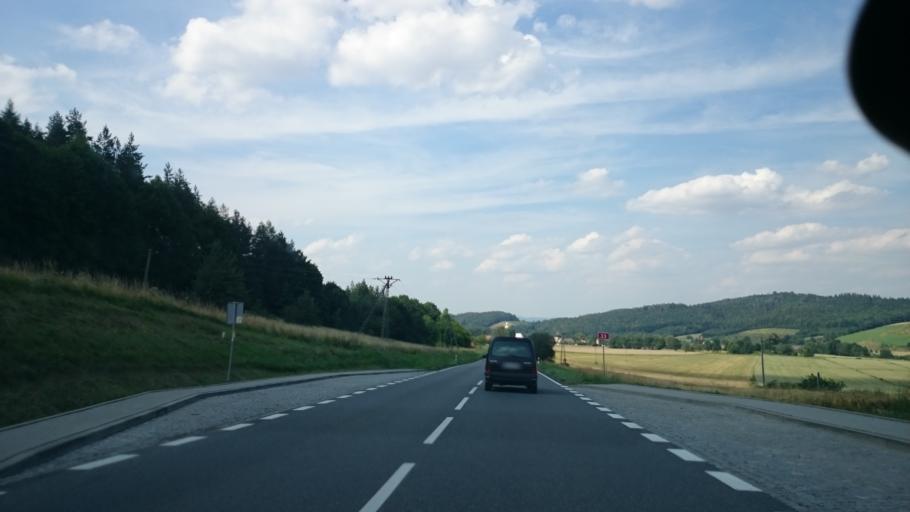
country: PL
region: Lower Silesian Voivodeship
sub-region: Powiat klodzki
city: Bystrzyca Klodzka
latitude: 50.3594
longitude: 16.6723
